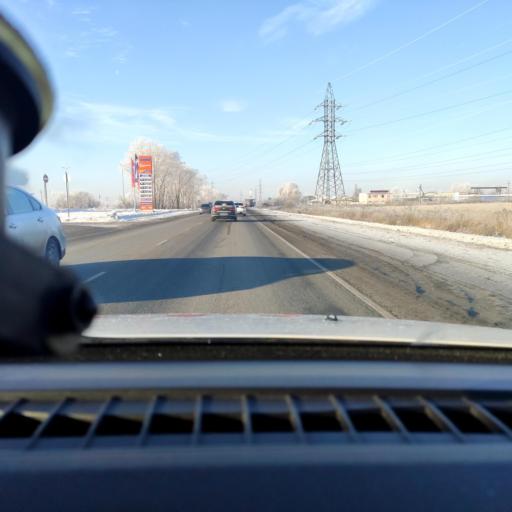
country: RU
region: Samara
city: Samara
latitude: 53.1286
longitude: 50.1556
